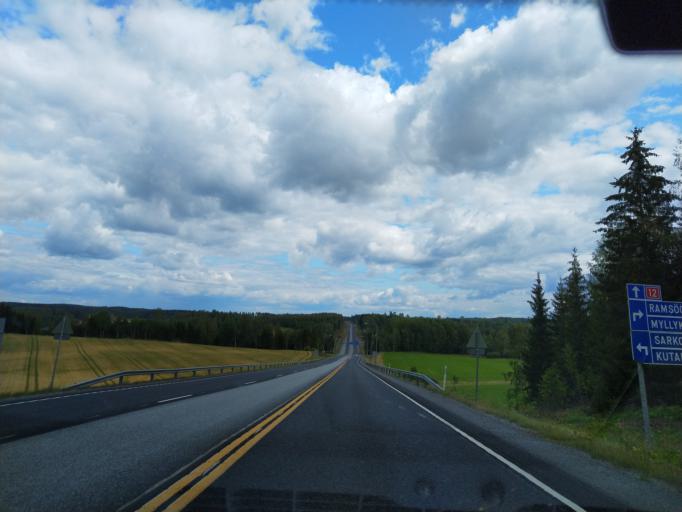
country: FI
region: Pirkanmaa
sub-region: Tampere
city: Haemeenkyroe
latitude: 61.3975
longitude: 23.2466
